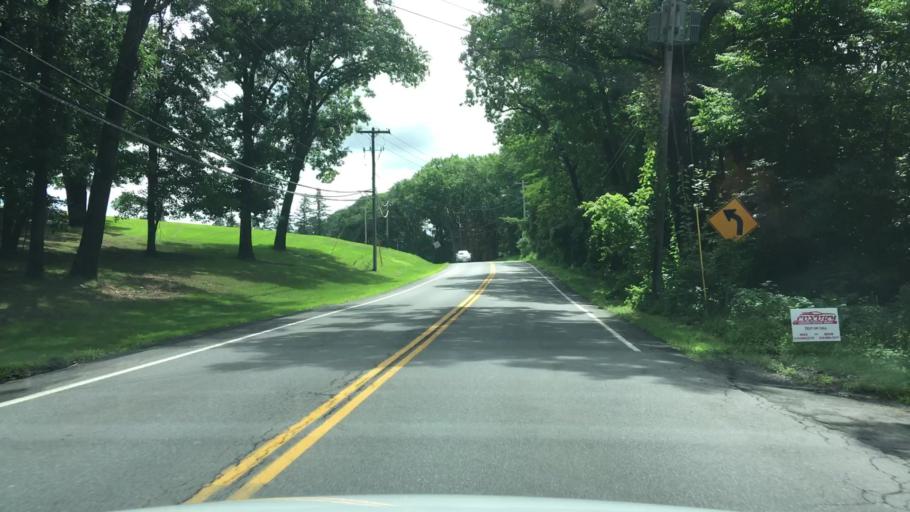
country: US
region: New York
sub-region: Albany County
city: Colonie
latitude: 42.7411
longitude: -73.8342
